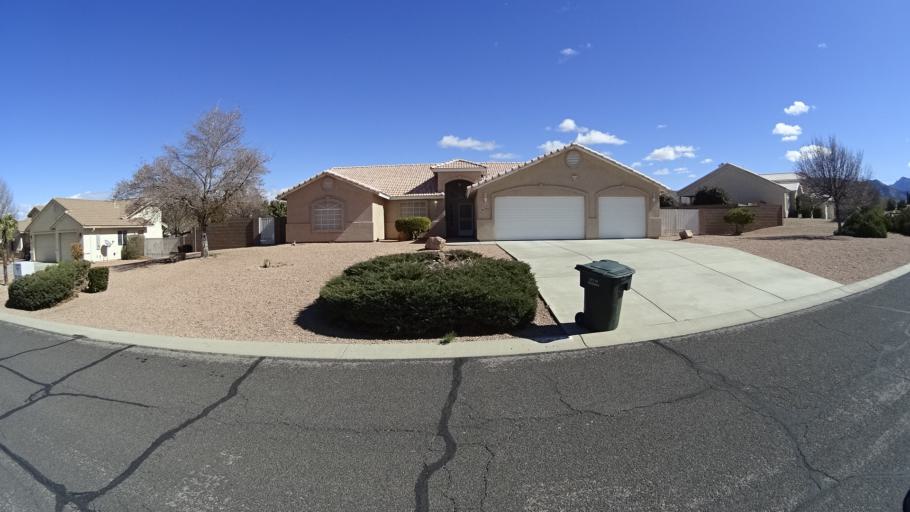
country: US
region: Arizona
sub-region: Mohave County
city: Kingman
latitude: 35.2046
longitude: -113.9719
